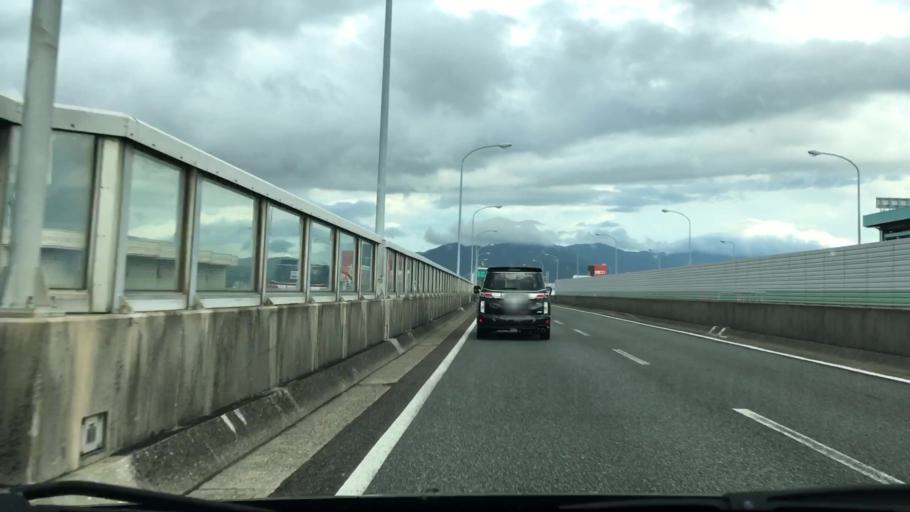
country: JP
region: Fukuoka
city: Fukuoka-shi
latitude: 33.6317
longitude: 130.4351
